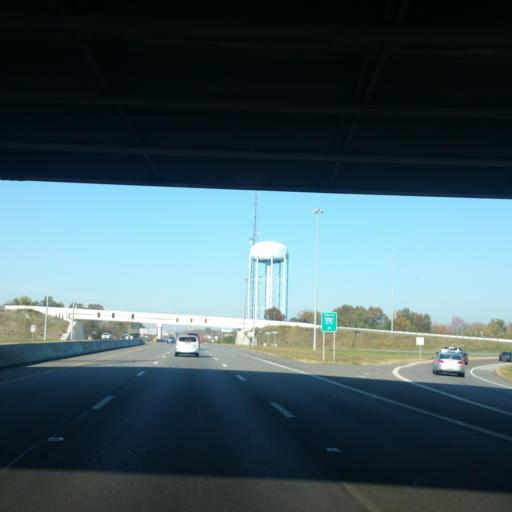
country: US
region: Ohio
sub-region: Clermont County
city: Summerside
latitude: 39.1017
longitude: -84.2843
